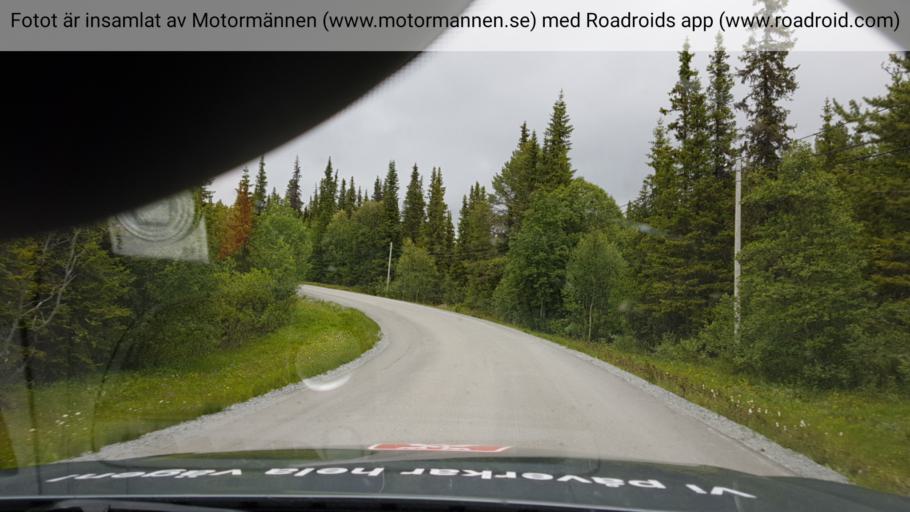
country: SE
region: Jaemtland
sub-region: Are Kommun
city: Are
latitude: 62.8619
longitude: 12.7642
